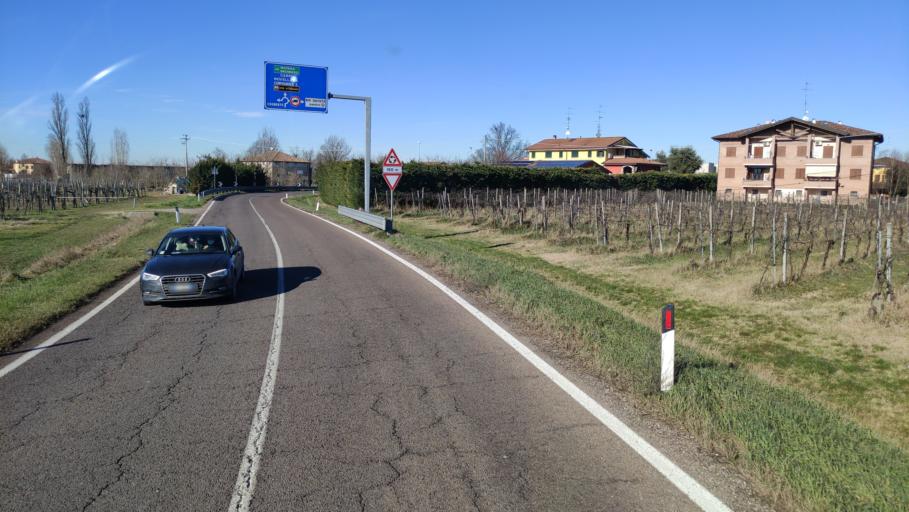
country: IT
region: Emilia-Romagna
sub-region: Provincia di Reggio Emilia
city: Rio Saliceto
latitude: 44.8076
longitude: 10.7836
